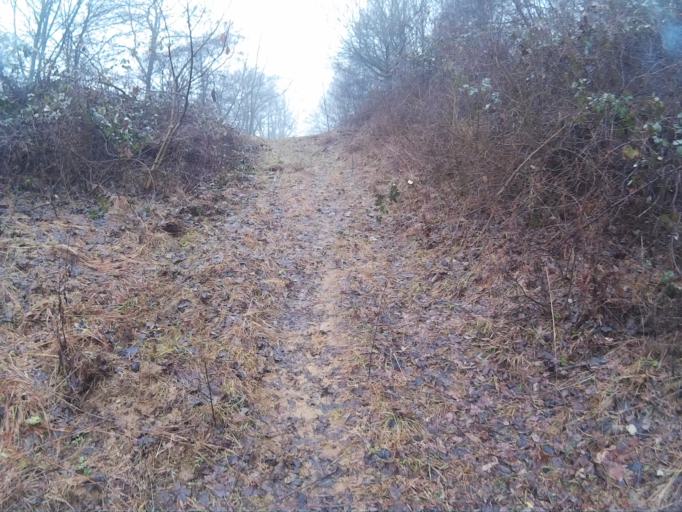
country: HU
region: Nograd
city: Somoskoujfalu
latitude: 48.1522
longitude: 19.8113
